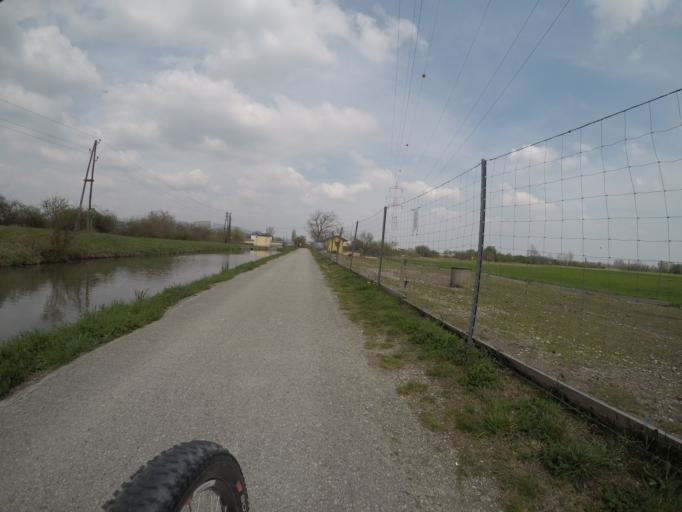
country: AT
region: Lower Austria
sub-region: Politischer Bezirk Baden
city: Kottingbrunn
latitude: 47.9731
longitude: 16.2469
